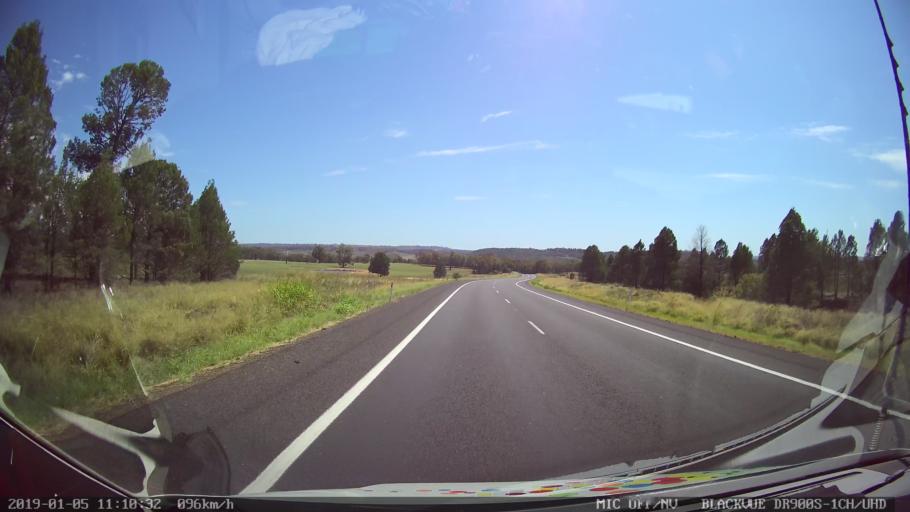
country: AU
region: New South Wales
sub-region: Warrumbungle Shire
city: Coonabarabran
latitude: -31.4054
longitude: 149.2452
